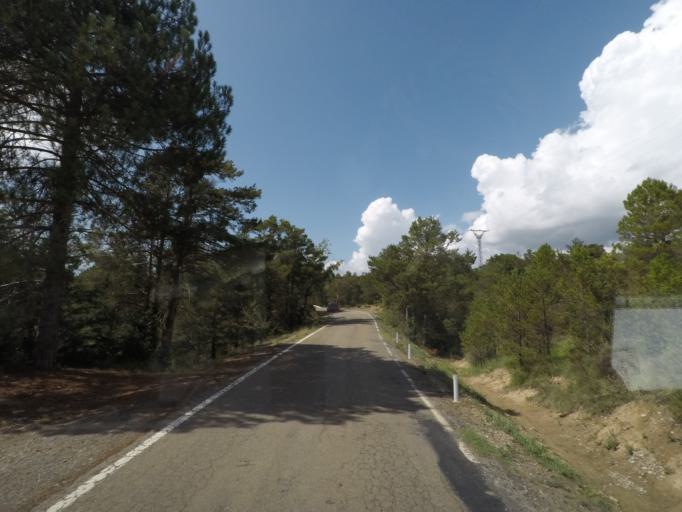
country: ES
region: Aragon
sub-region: Provincia de Huesca
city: Yebra de Basa
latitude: 42.4021
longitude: -0.3584
